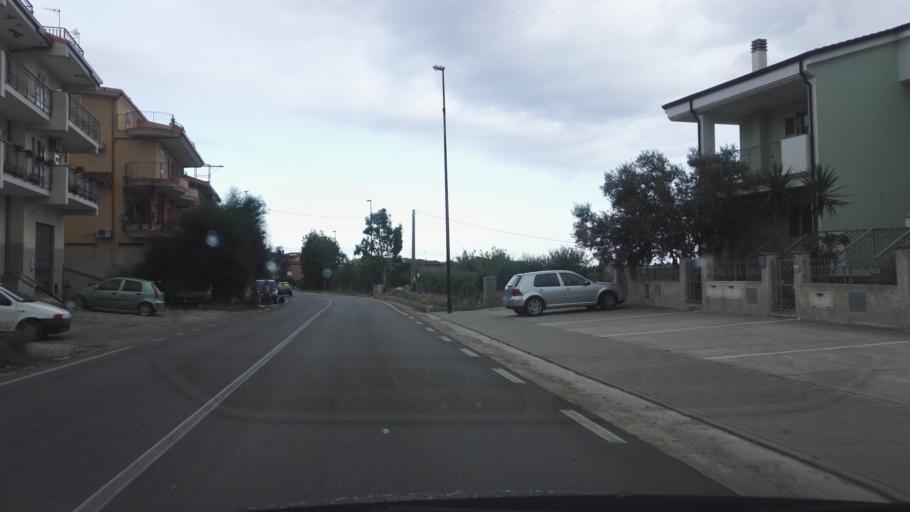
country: IT
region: Calabria
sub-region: Provincia di Catanzaro
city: Badolato Marina
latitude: 38.5722
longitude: 16.5595
